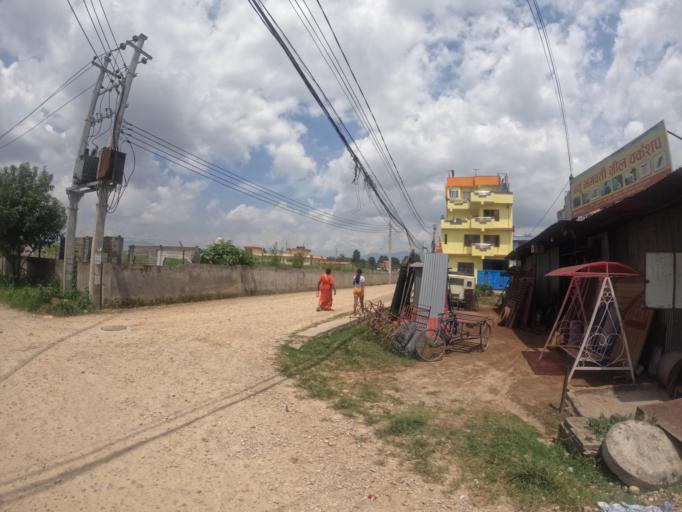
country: NP
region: Central Region
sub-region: Bagmati Zone
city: Bhaktapur
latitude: 27.6764
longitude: 85.3794
